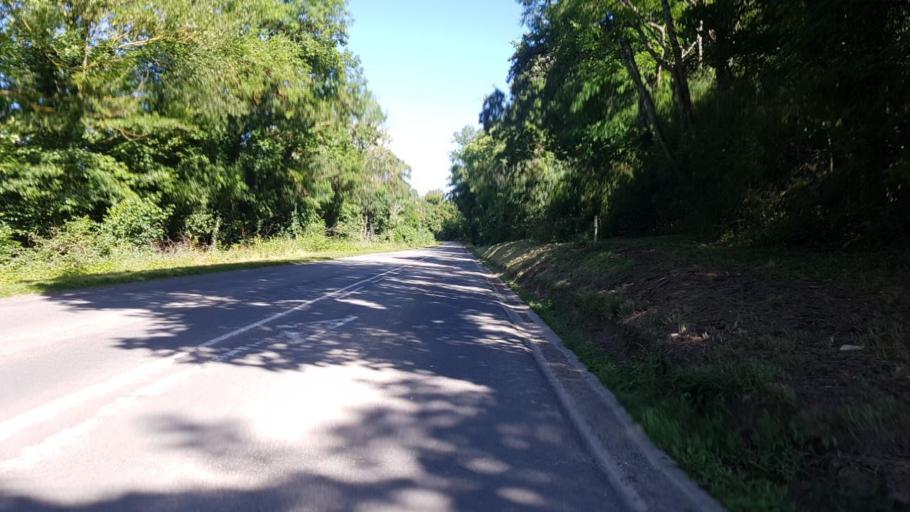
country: FR
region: Picardie
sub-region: Departement de l'Aisne
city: Charly-sur-Marne
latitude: 48.9734
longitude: 3.2531
